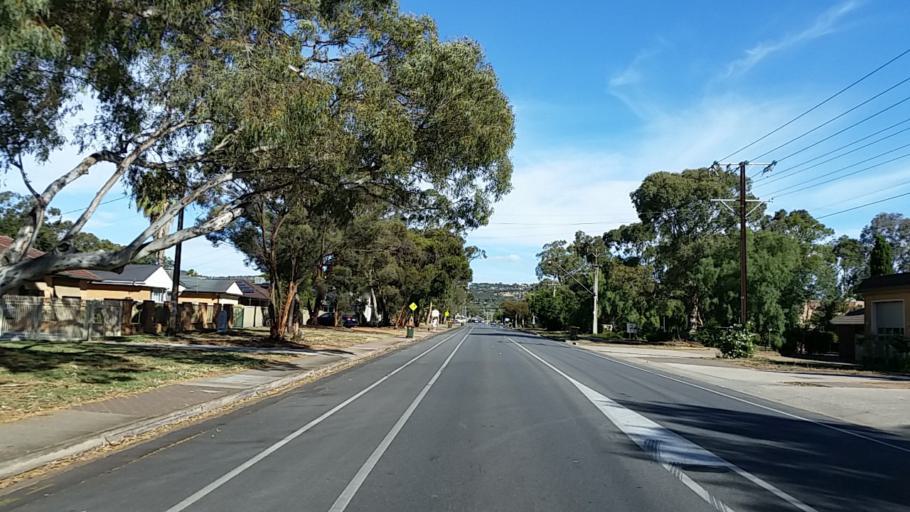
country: AU
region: South Australia
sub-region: Salisbury
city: Salisbury
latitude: -34.7809
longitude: 138.6506
